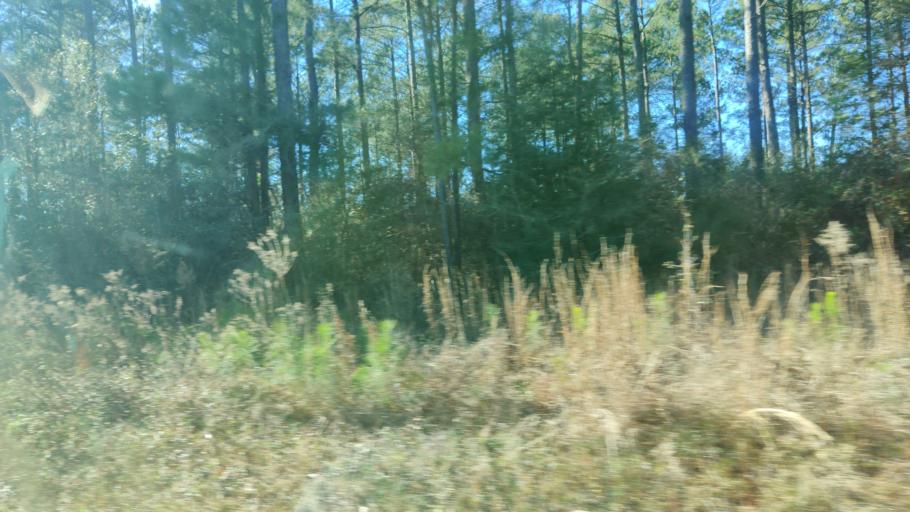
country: US
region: Mississippi
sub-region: Jones County
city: Ellisville
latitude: 31.5486
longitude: -89.3308
